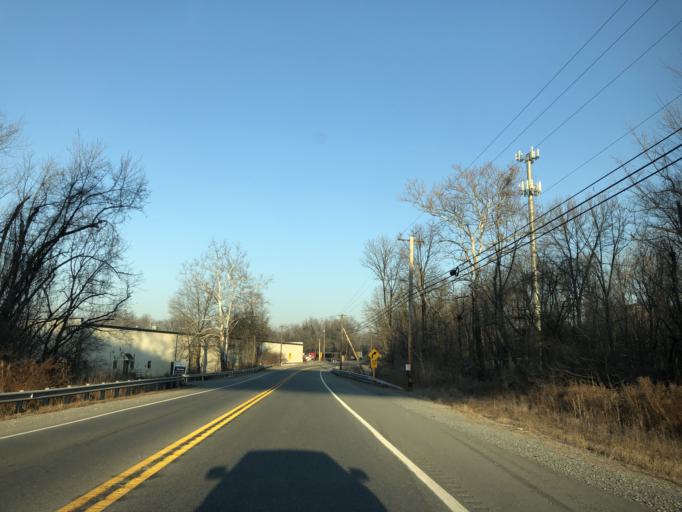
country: US
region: Pennsylvania
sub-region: Chester County
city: Downingtown
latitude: 39.9953
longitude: -75.6999
